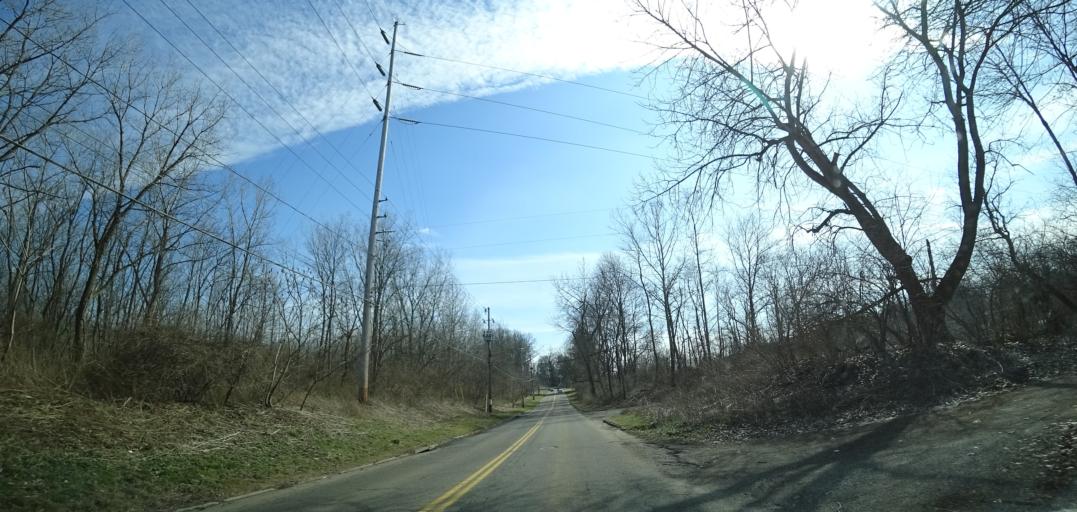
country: US
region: Ohio
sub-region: Summit County
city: Akron
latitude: 41.1165
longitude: -81.5252
